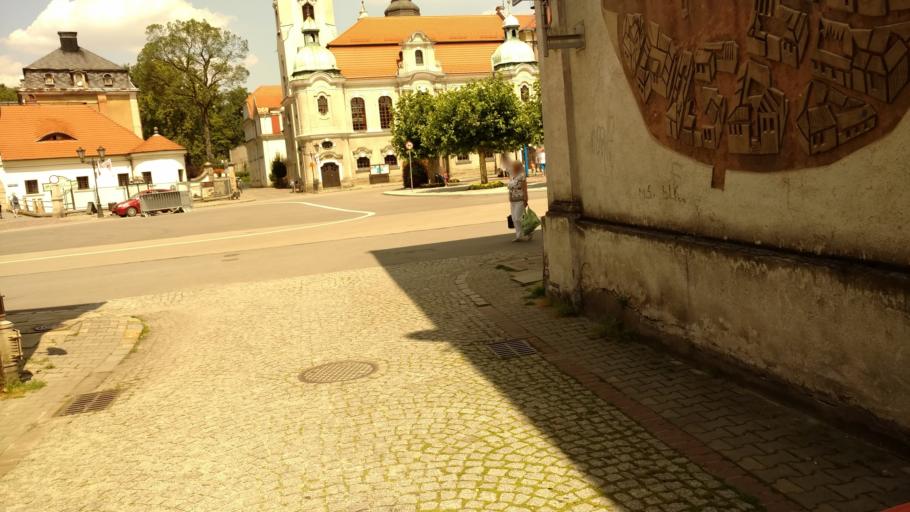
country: PL
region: Silesian Voivodeship
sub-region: Powiat pszczynski
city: Pszczyna
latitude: 49.9773
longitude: 18.9417
